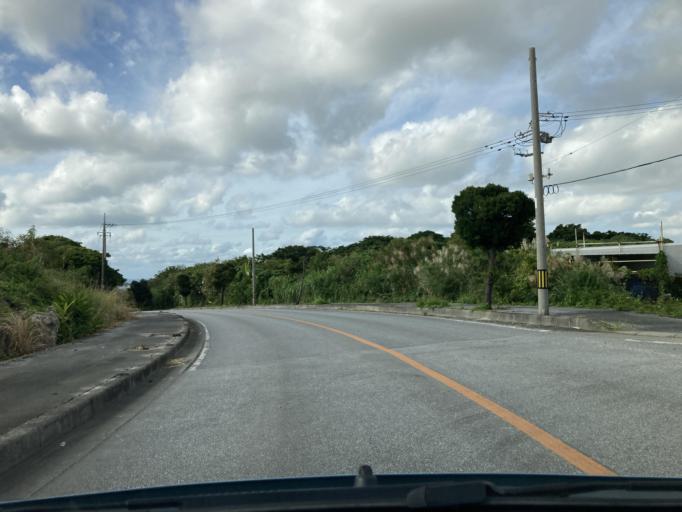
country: JP
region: Okinawa
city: Itoman
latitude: 26.1265
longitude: 127.7133
